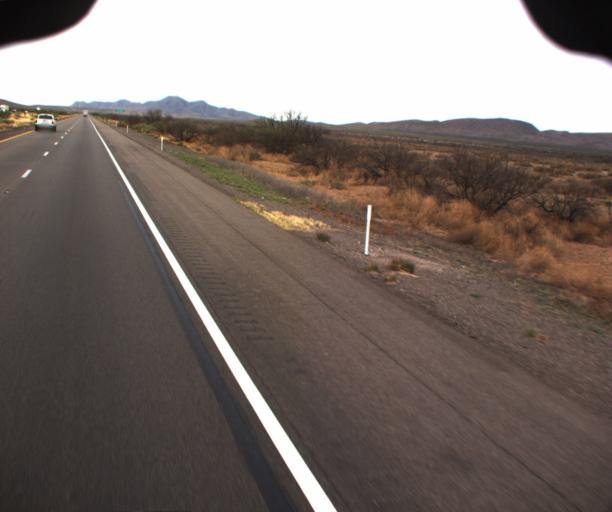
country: US
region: Arizona
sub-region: Cochise County
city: Willcox
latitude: 32.1713
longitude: -109.9585
